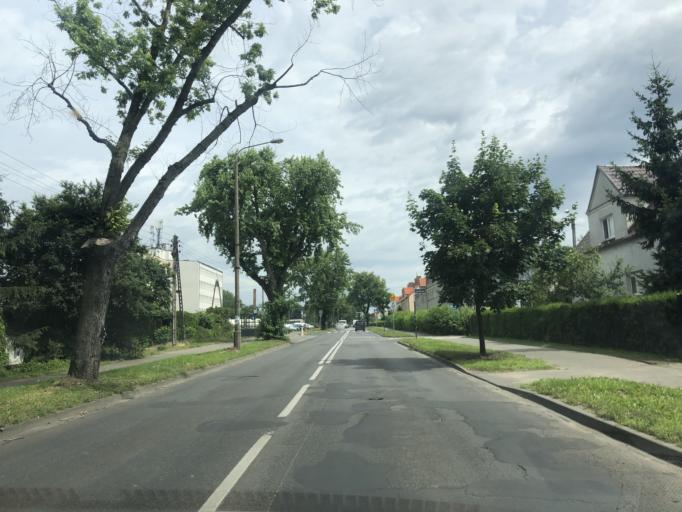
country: PL
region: Greater Poland Voivodeship
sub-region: Powiat poznanski
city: Lubon
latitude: 52.3649
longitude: 16.8939
